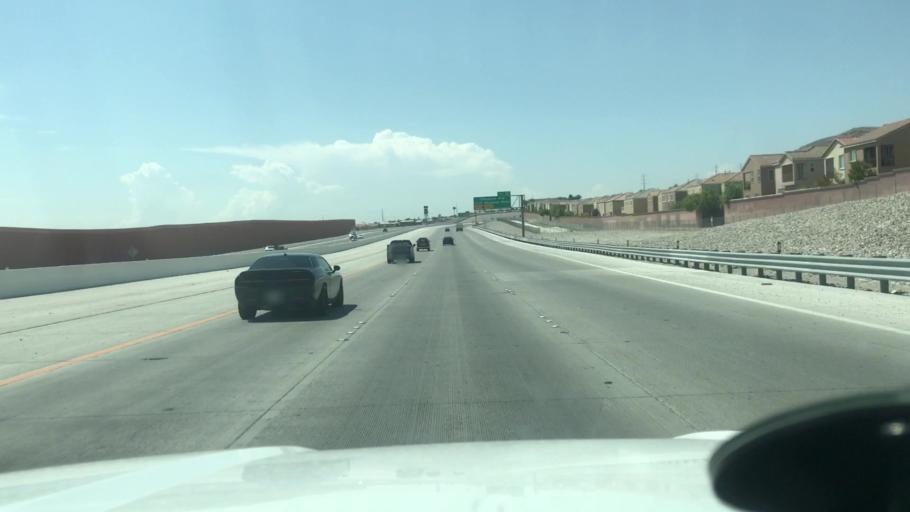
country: US
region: Nevada
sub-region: Clark County
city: Summerlin South
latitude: 36.2305
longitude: -115.3257
